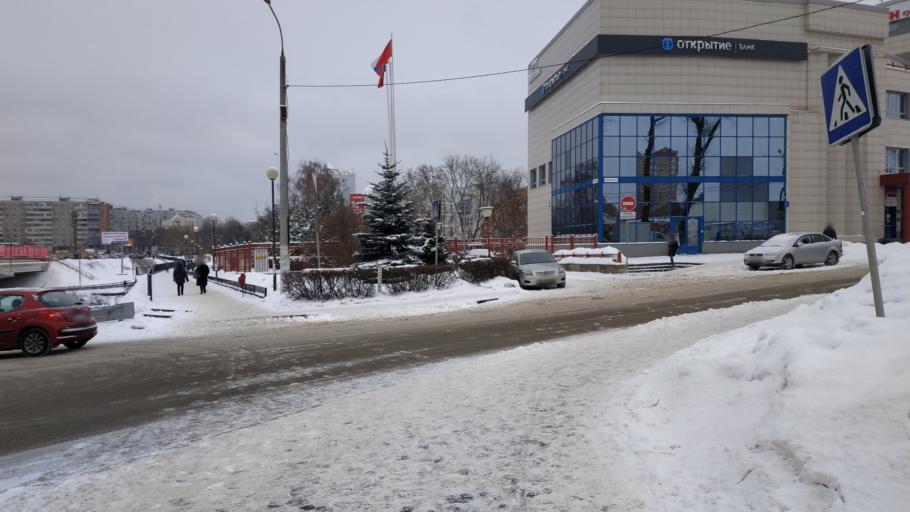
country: RU
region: Moskovskaya
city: Shchelkovo
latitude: 55.9216
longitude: 37.9992
